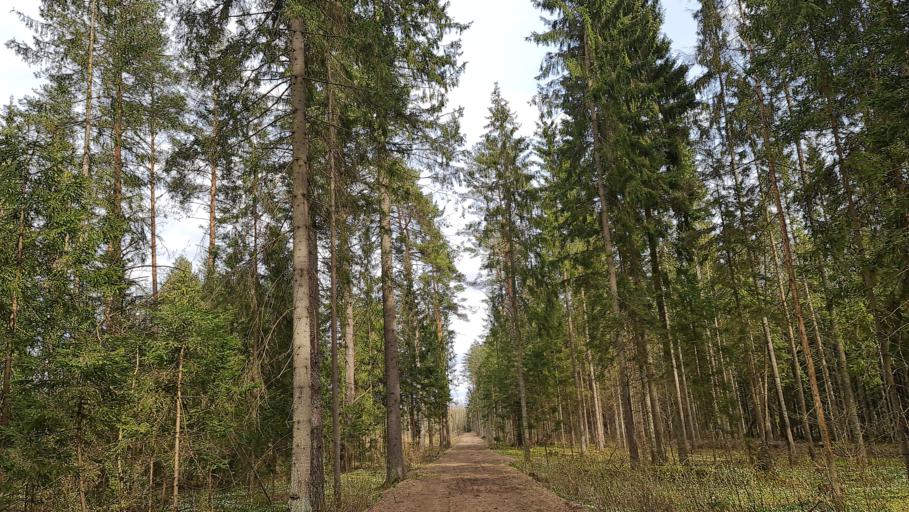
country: BY
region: Vitebsk
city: Byahoml'
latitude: 54.7495
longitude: 28.0442
